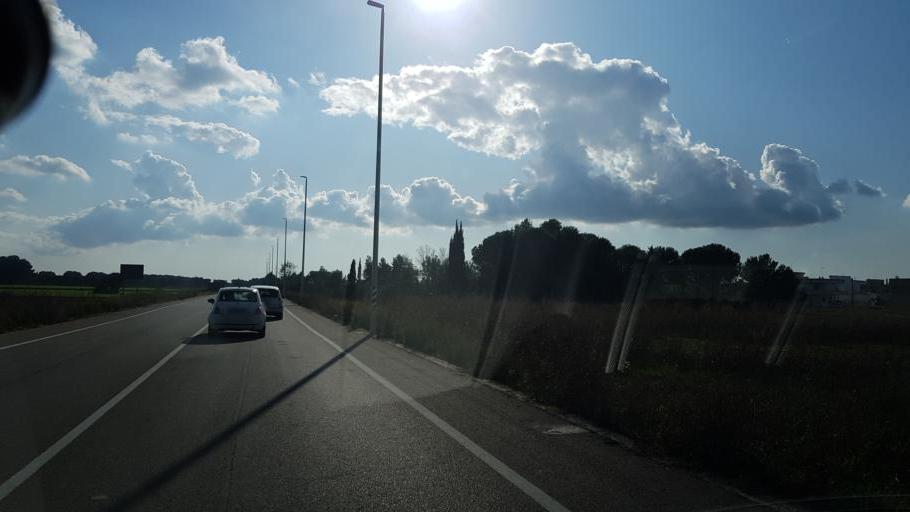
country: IT
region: Apulia
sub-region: Provincia di Lecce
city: Salice Salentino
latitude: 40.3793
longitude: 17.9697
